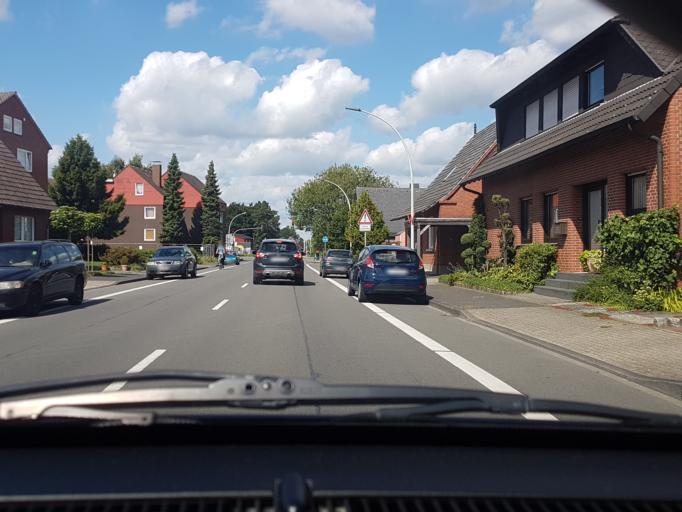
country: DE
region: North Rhine-Westphalia
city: Emsdetten
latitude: 52.1675
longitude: 7.5058
